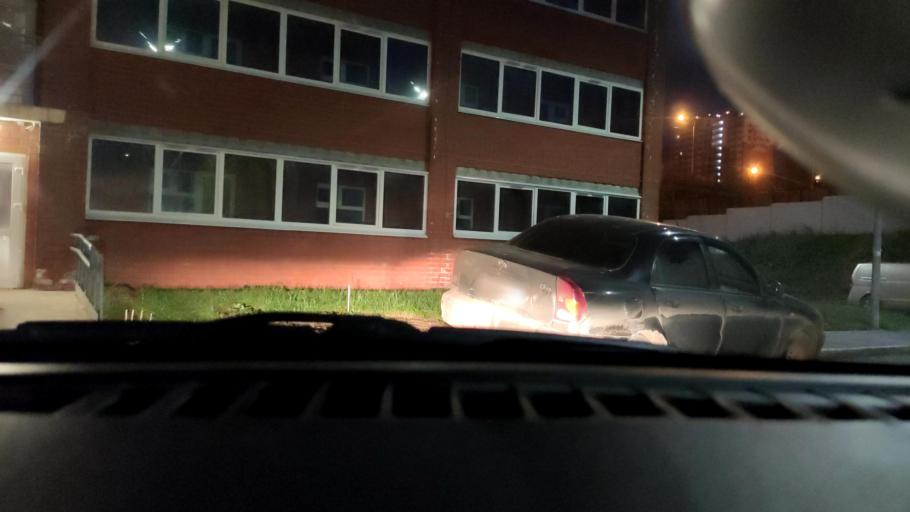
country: RU
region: Perm
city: Perm
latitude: 57.9861
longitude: 56.2309
